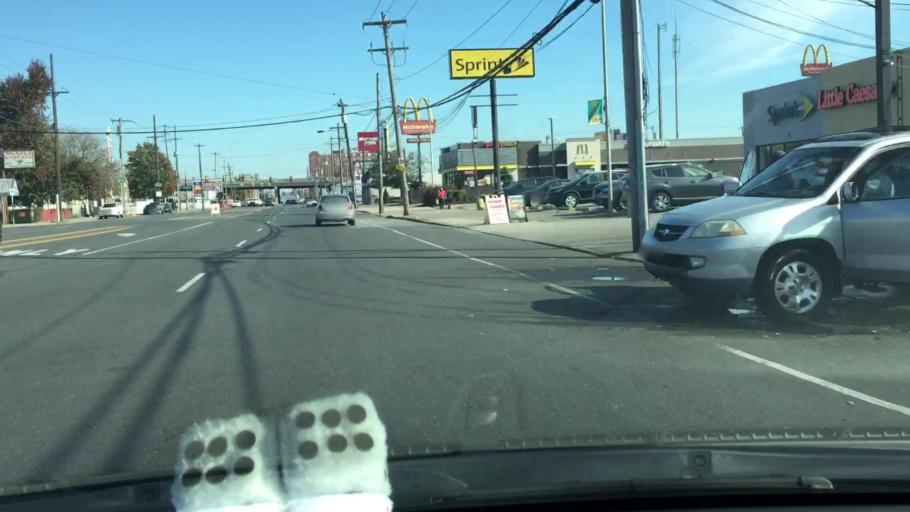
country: US
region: New Jersey
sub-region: Camden County
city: Camden
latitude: 39.9143
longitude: -75.1523
